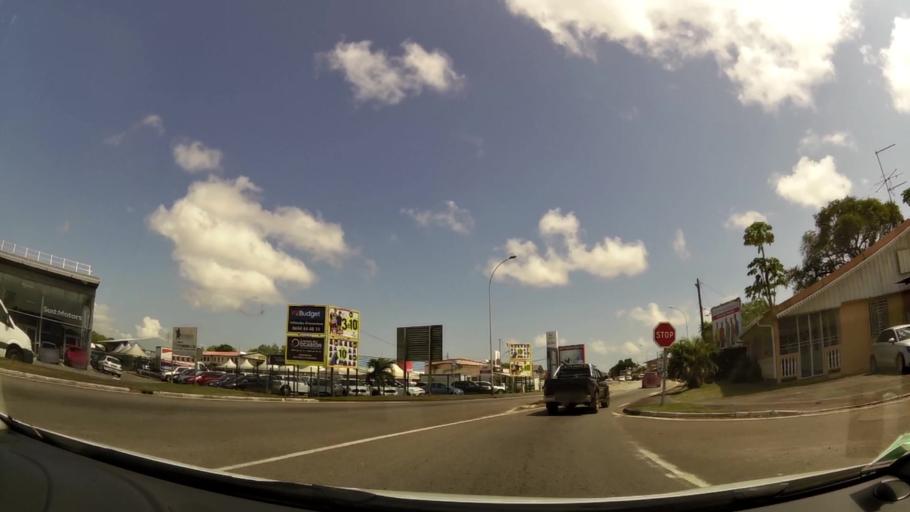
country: GF
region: Guyane
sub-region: Guyane
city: Cayenne
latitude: 4.9257
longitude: -52.3242
